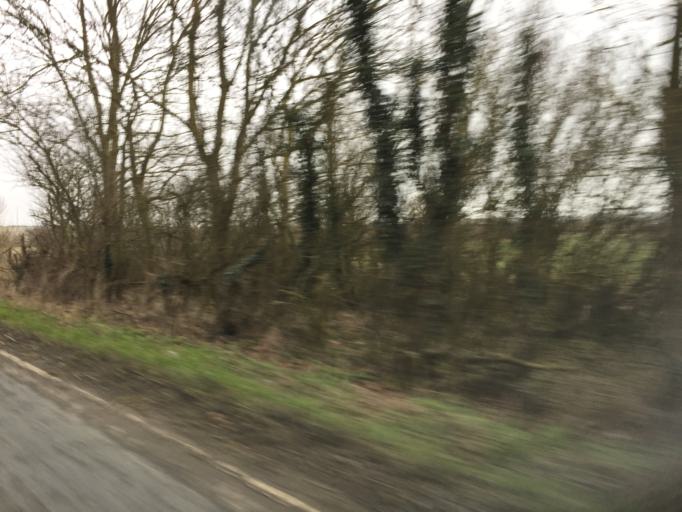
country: GB
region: England
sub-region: Oxfordshire
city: Wantage
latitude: 51.6013
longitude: -1.4709
